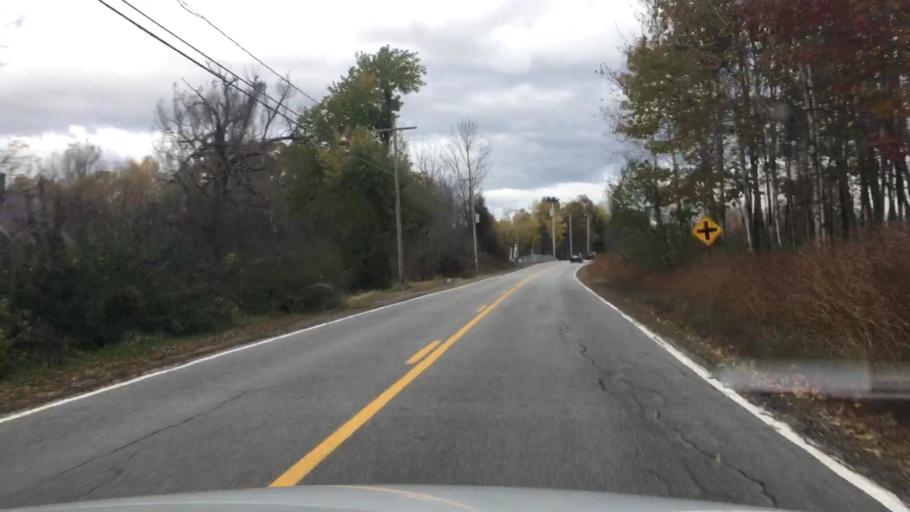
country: US
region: Maine
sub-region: Androscoggin County
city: Sabattus
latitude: 44.1709
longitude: -70.0719
